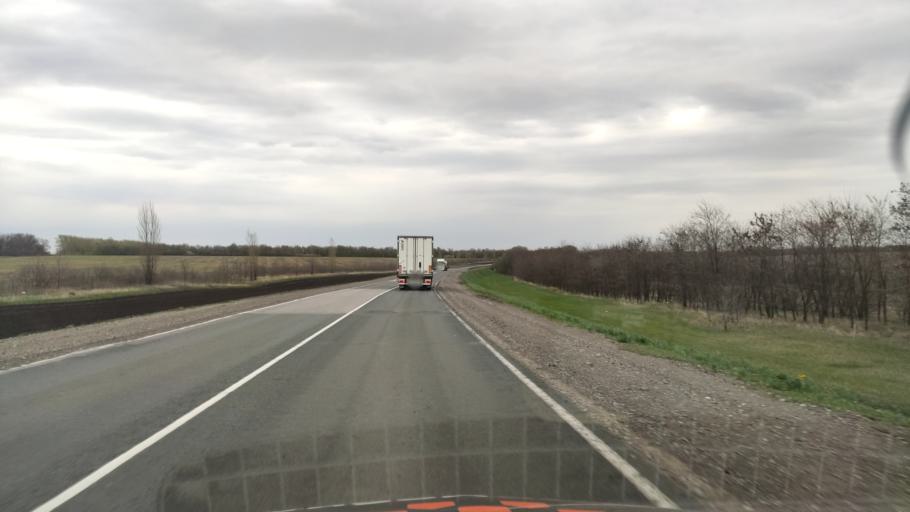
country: RU
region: Voronezj
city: Nizhnedevitsk
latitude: 51.5765
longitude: 38.3109
